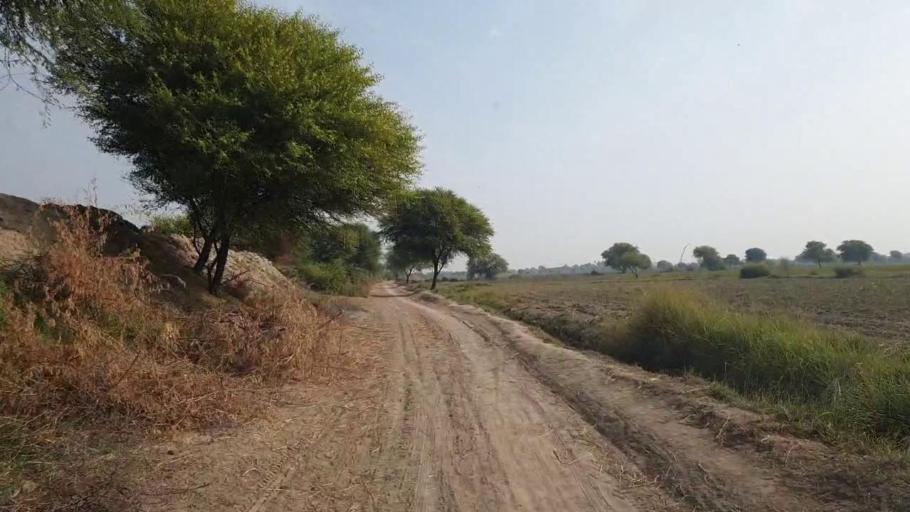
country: PK
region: Sindh
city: Talhar
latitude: 24.9006
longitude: 68.8925
